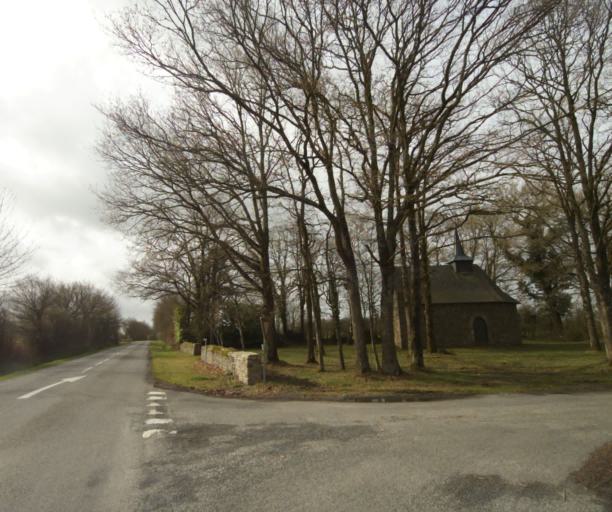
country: FR
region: Pays de la Loire
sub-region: Departement de la Loire-Atlantique
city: Bouvron
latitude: 47.4053
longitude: -1.8868
